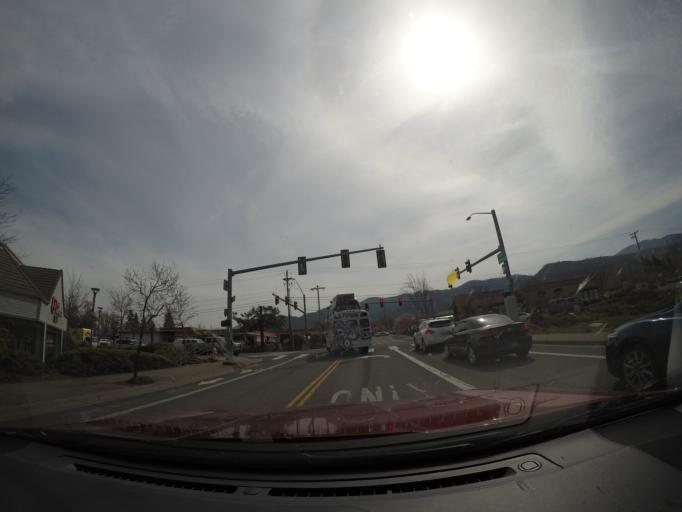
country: US
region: Oregon
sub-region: Jackson County
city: Ashland
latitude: 42.1856
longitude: -122.6715
